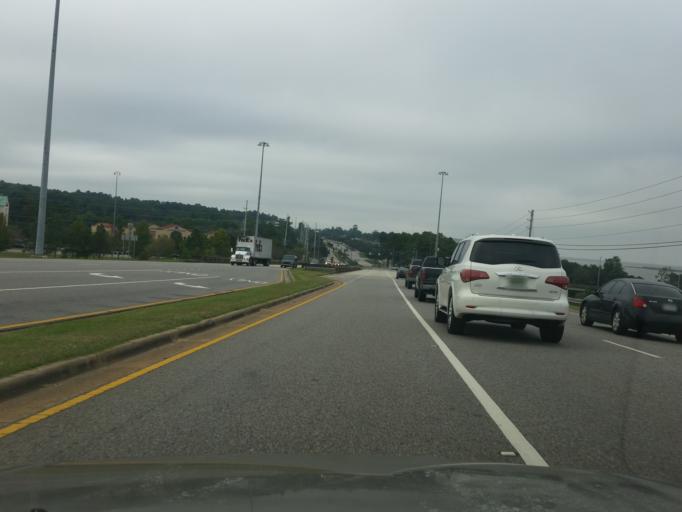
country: US
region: Alabama
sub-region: Baldwin County
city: Spanish Fort
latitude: 30.6573
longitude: -87.9116
